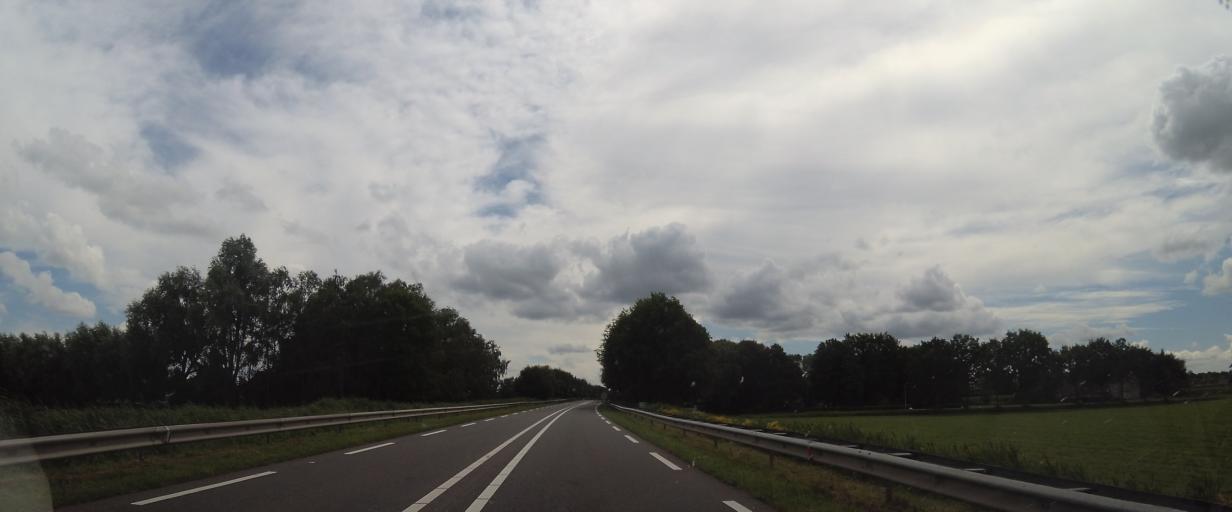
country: NL
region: North Brabant
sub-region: Gemeente Breda
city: Hoge Vucht
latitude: 51.6409
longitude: 4.7678
